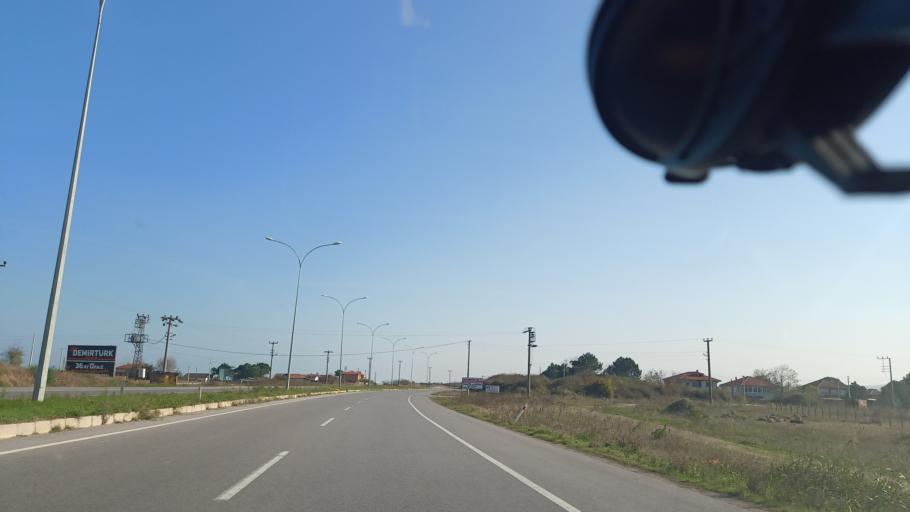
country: TR
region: Sakarya
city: Karasu
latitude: 41.0871
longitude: 30.7471
